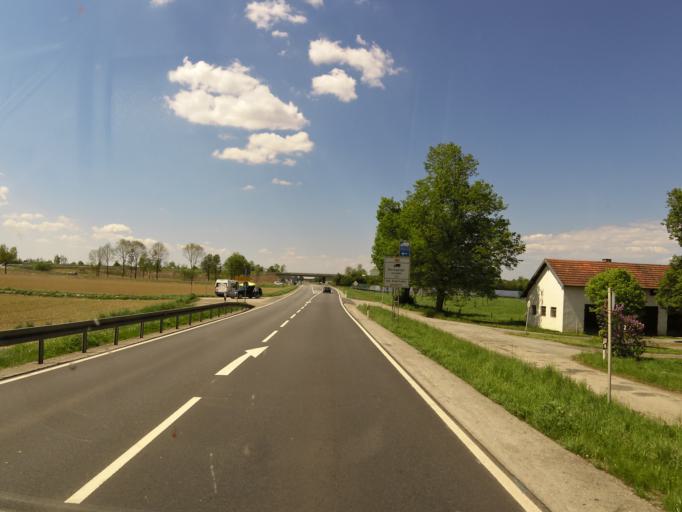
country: DE
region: Bavaria
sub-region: Lower Bavaria
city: Plattling
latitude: 48.7902
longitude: 12.8393
